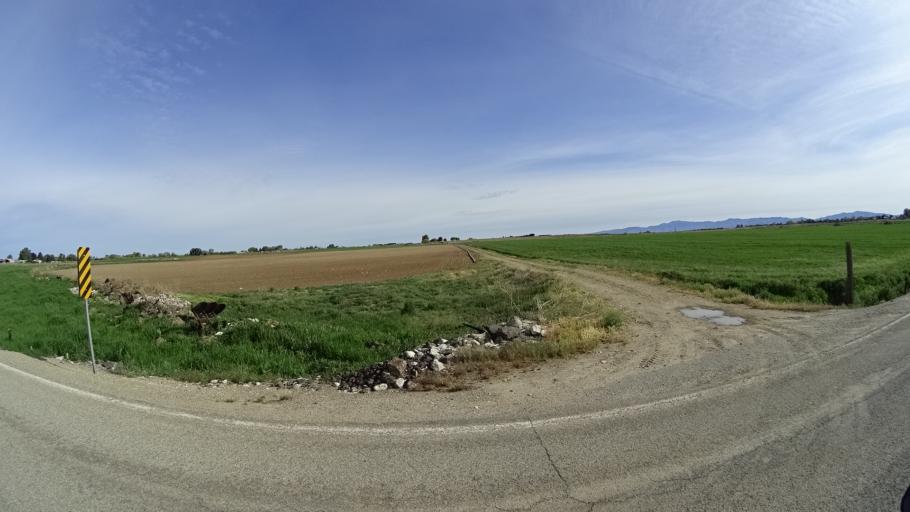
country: US
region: Idaho
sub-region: Ada County
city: Kuna
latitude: 43.4736
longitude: -116.3468
